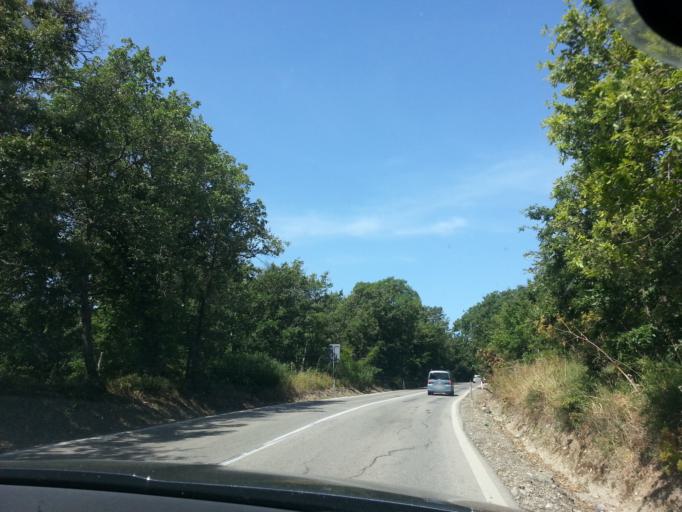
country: IT
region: Latium
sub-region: Provincia di Viterbo
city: Monte Romano
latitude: 42.2597
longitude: 11.8358
